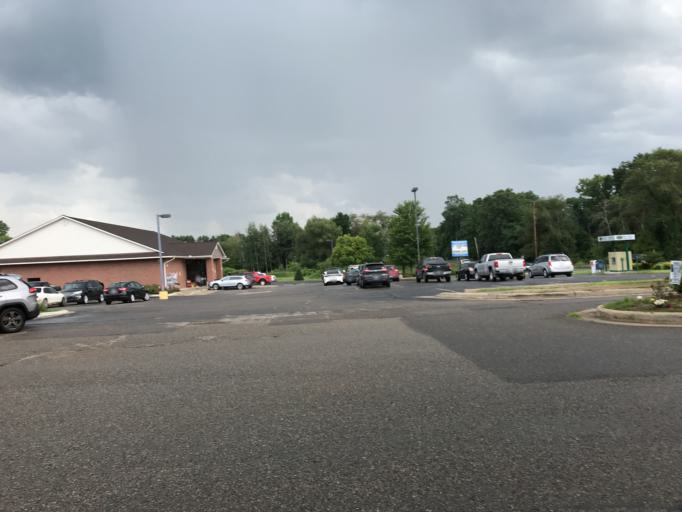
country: US
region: Michigan
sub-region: Oakland County
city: Milford
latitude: 42.5590
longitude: -83.6179
